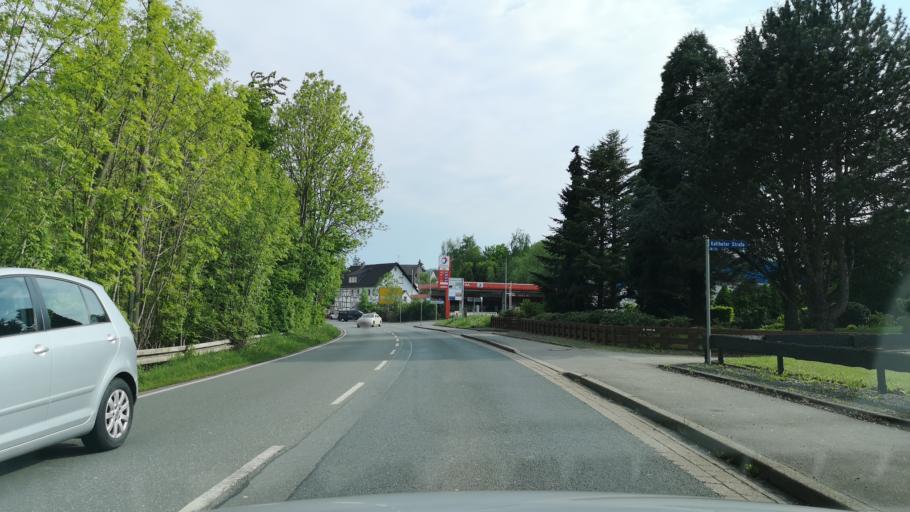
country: DE
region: North Rhine-Westphalia
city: Iserlohn
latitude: 51.4270
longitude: 7.6758
